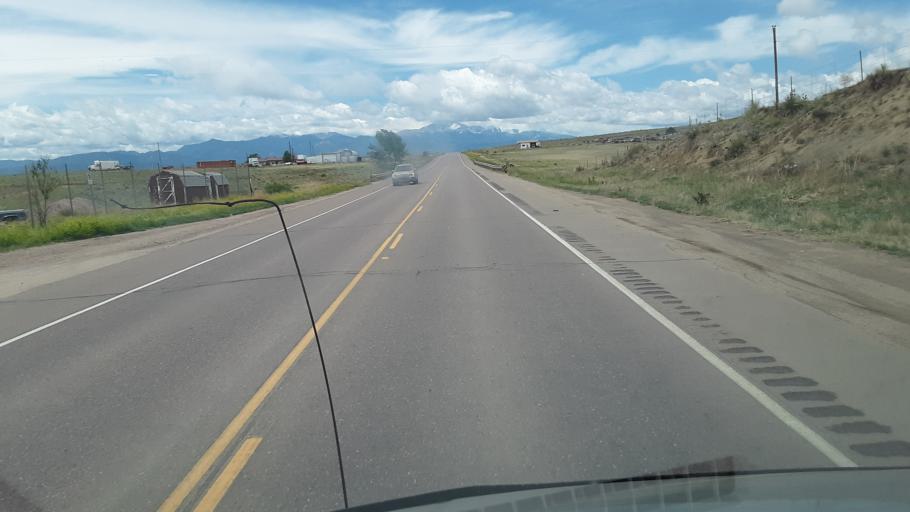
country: US
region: Colorado
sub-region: El Paso County
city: Cimarron Hills
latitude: 38.8387
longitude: -104.5967
